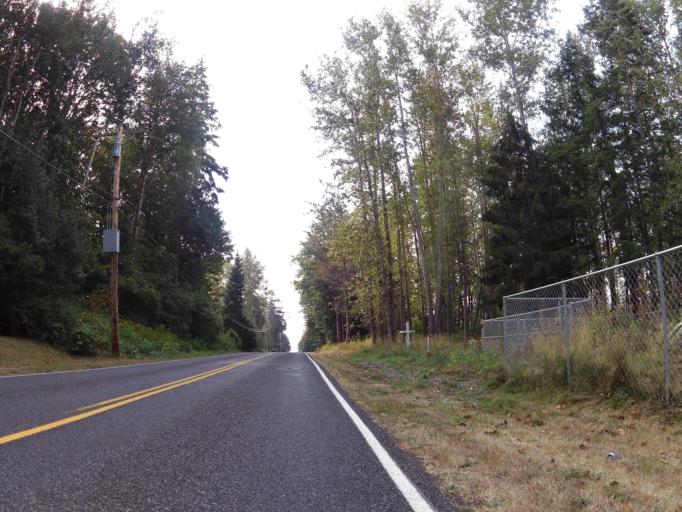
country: US
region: Washington
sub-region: Whatcom County
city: Ferndale
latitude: 48.8107
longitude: -122.6828
